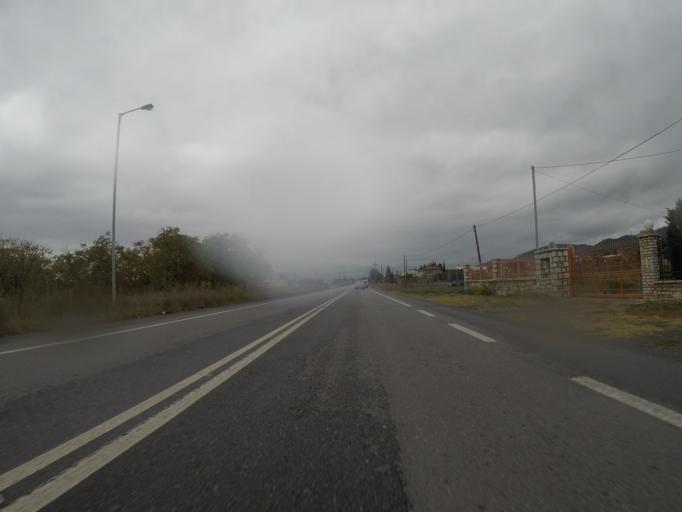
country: GR
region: Peloponnese
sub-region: Nomos Arkadias
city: Tripoli
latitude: 37.5423
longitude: 22.3922
